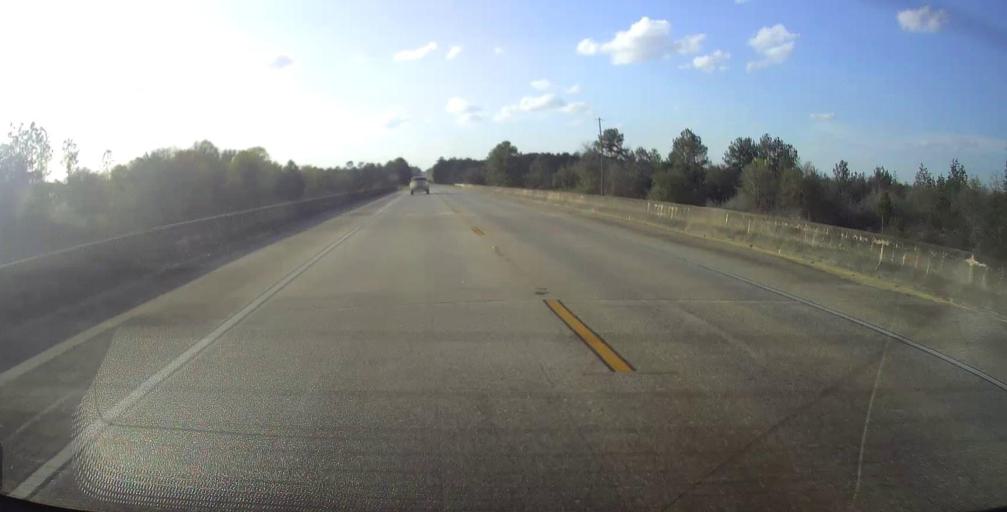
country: US
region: Georgia
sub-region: Tattnall County
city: Reidsville
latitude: 32.1177
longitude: -82.1900
